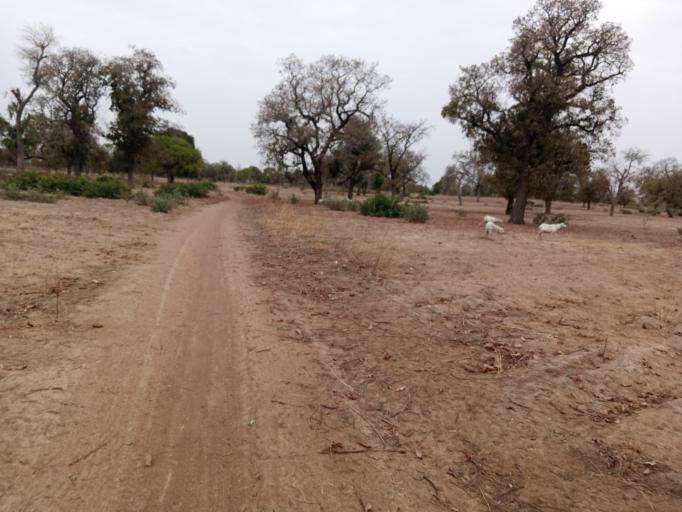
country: BF
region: Boucle du Mouhoun
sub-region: Province de la Kossi
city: Nouna
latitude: 12.7699
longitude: -4.0609
